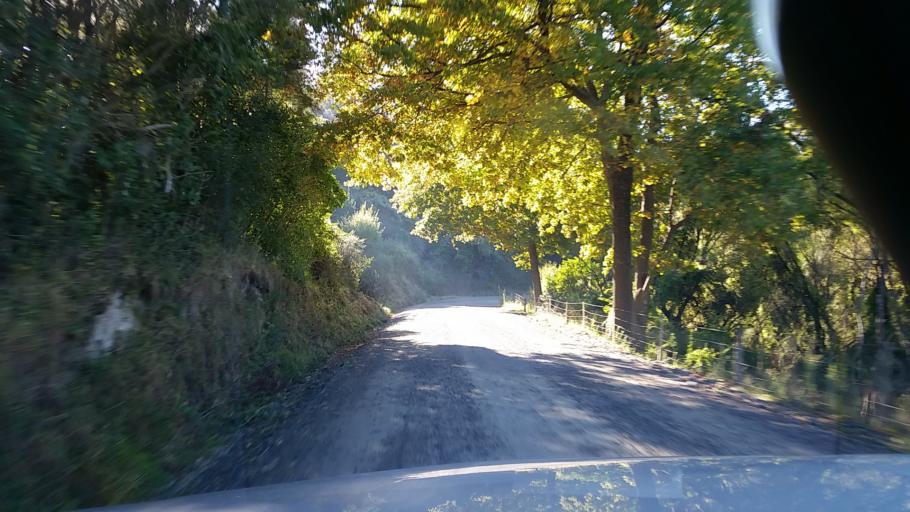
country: NZ
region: Marlborough
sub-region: Marlborough District
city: Blenheim
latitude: -41.4443
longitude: 173.8889
